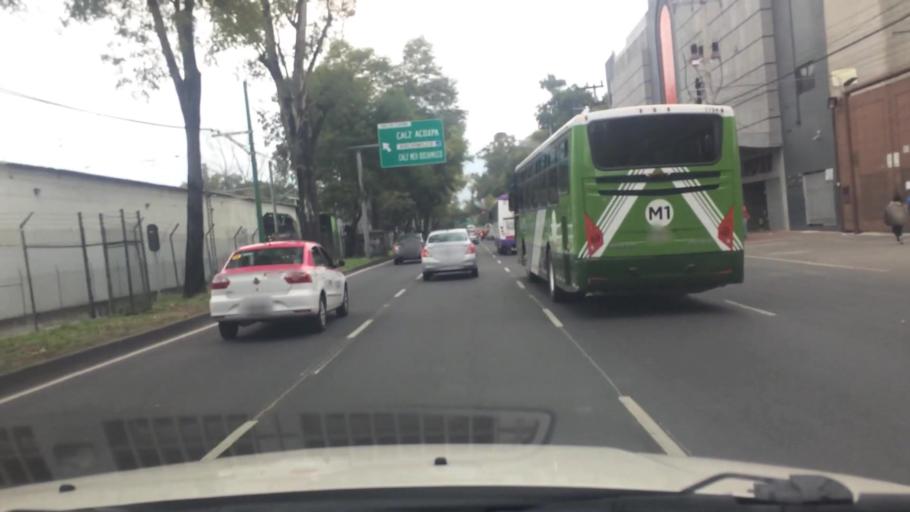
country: MX
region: Mexico City
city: Tlalpan
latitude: 19.3005
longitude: -99.1486
